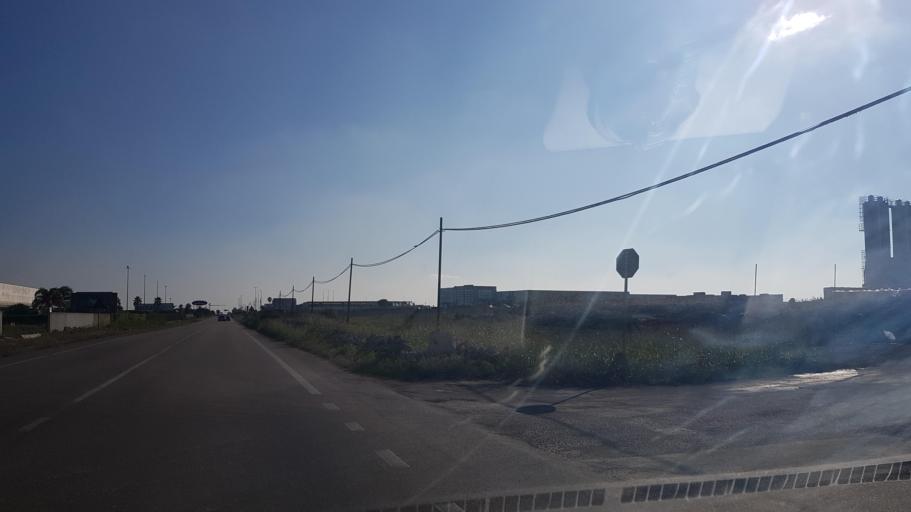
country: IT
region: Apulia
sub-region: Provincia di Lecce
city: Nociglia
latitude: 40.0182
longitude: 18.3243
